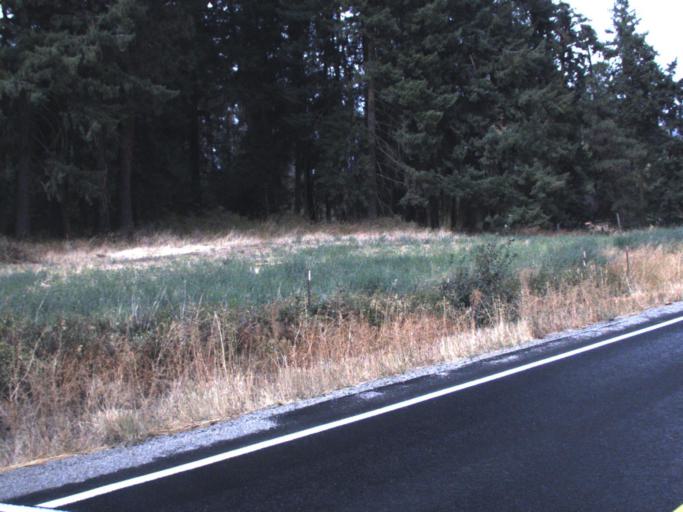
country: US
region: Washington
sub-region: Stevens County
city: Chewelah
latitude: 48.0736
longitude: -117.7613
